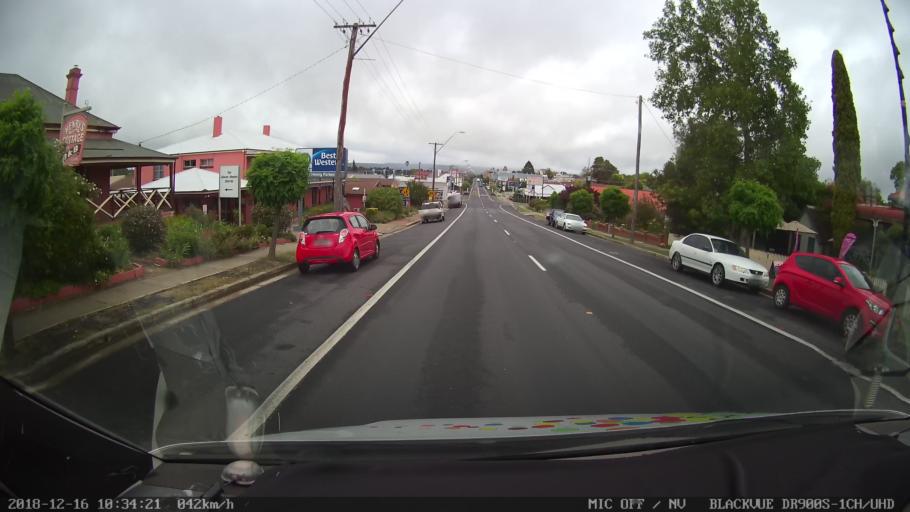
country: AU
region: New South Wales
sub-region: Tenterfield Municipality
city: Carrolls Creek
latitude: -29.0585
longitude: 152.0182
